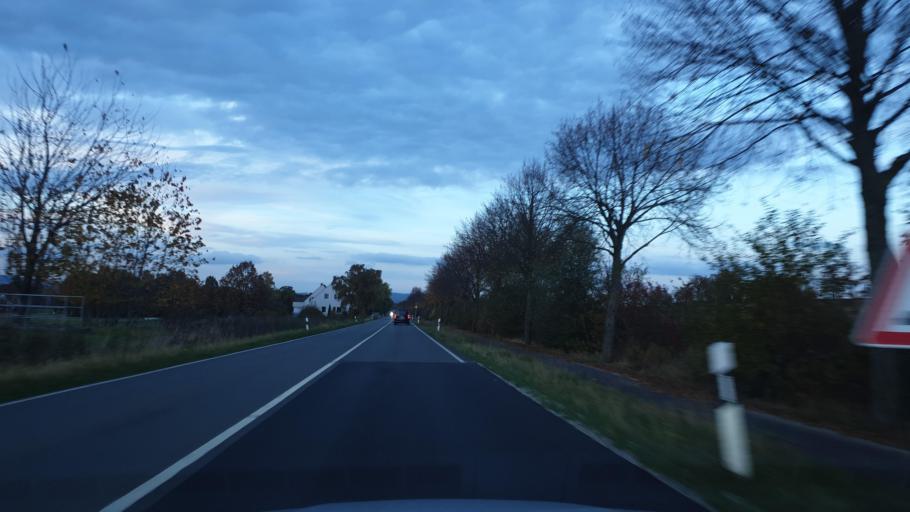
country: DE
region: North Rhine-Westphalia
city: Spenge
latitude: 52.1670
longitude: 8.5045
